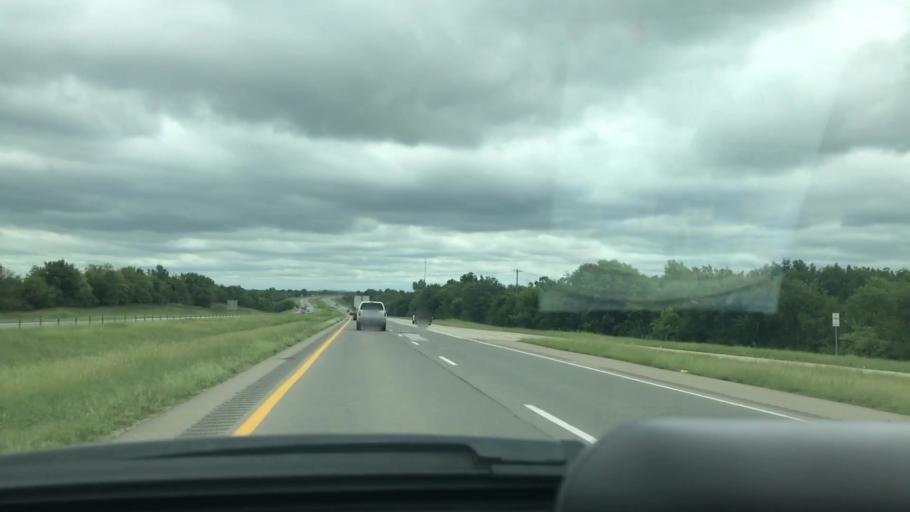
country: US
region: Oklahoma
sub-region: McIntosh County
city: Checotah
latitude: 35.4772
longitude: -95.5351
